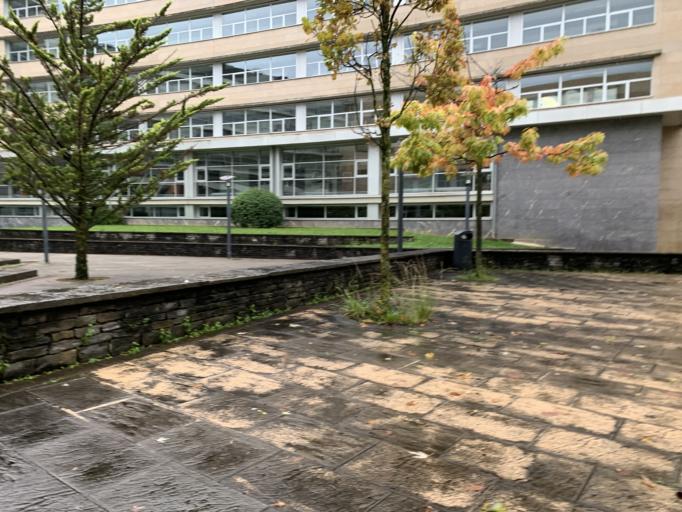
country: ES
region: Basque Country
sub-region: Provincia de Guipuzcoa
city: San Sebastian
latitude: 43.3098
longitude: -2.0095
